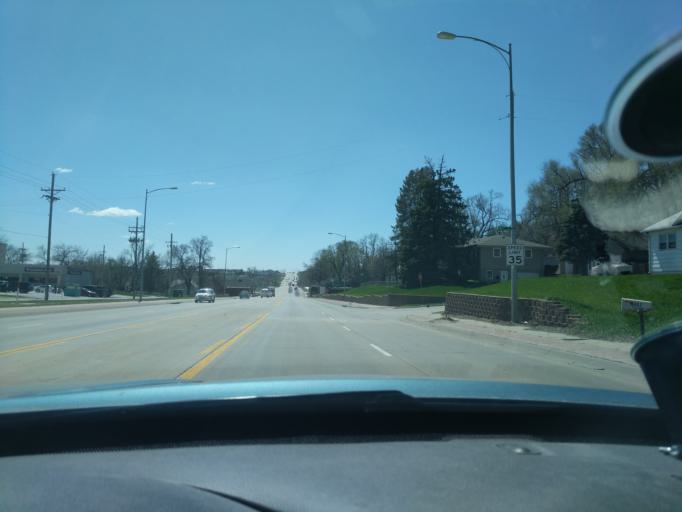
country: US
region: Nebraska
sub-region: Douglas County
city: Elkhorn
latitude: 41.2859
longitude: -96.2345
